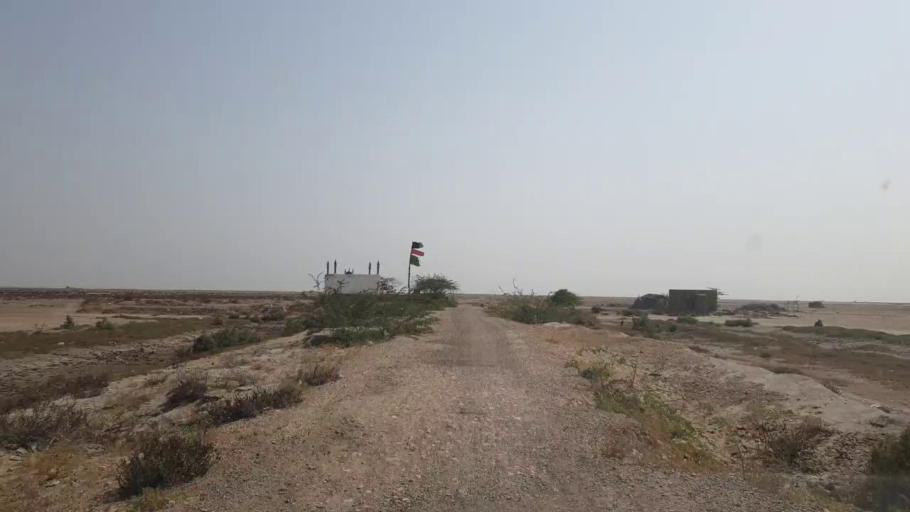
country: PK
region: Sindh
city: Jati
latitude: 24.3371
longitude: 68.6049
